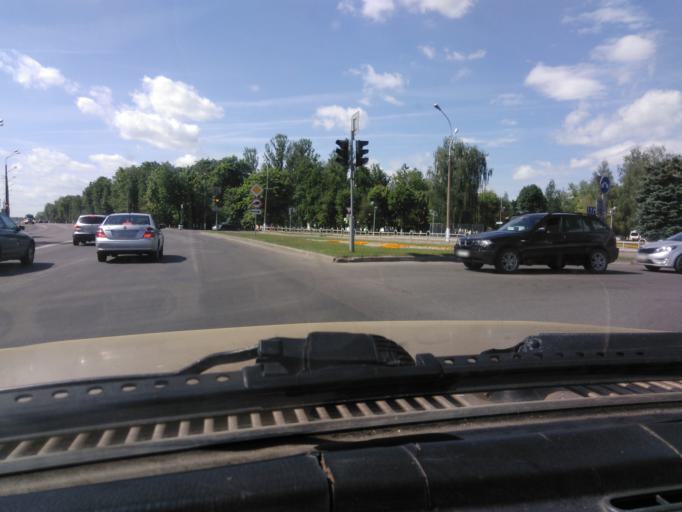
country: BY
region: Mogilev
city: Mahilyow
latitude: 53.9166
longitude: 30.3134
